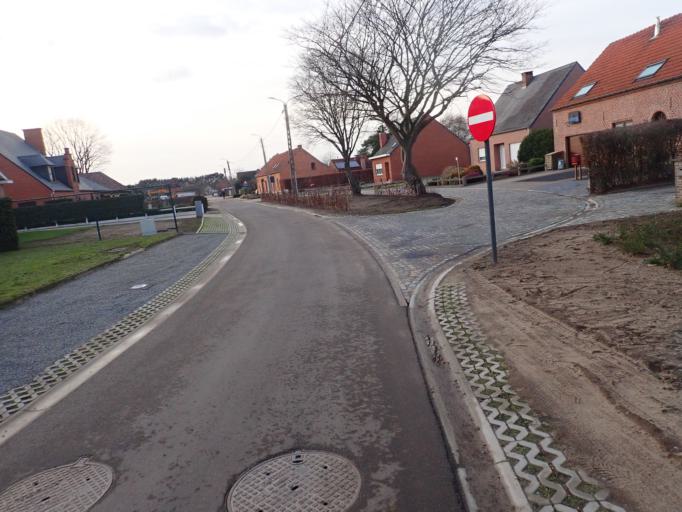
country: BE
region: Flanders
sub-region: Provincie Vlaams-Brabant
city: Rotselaar
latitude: 50.9728
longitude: 4.7131
